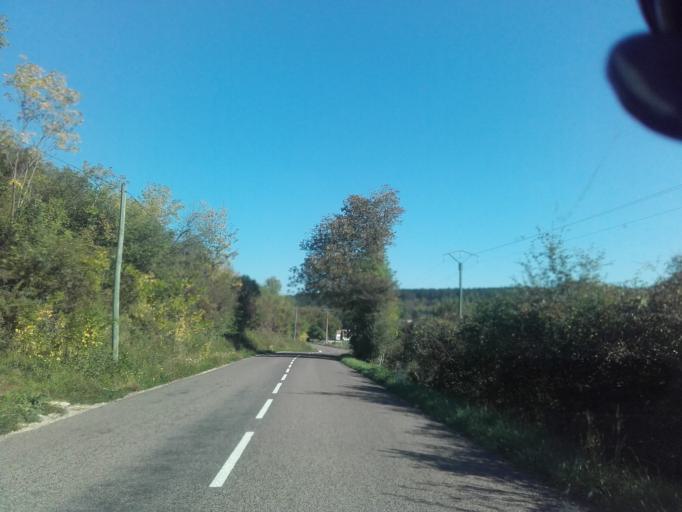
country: FR
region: Bourgogne
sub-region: Departement de la Cote-d'Or
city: Meursault
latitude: 47.0189
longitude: 4.7626
